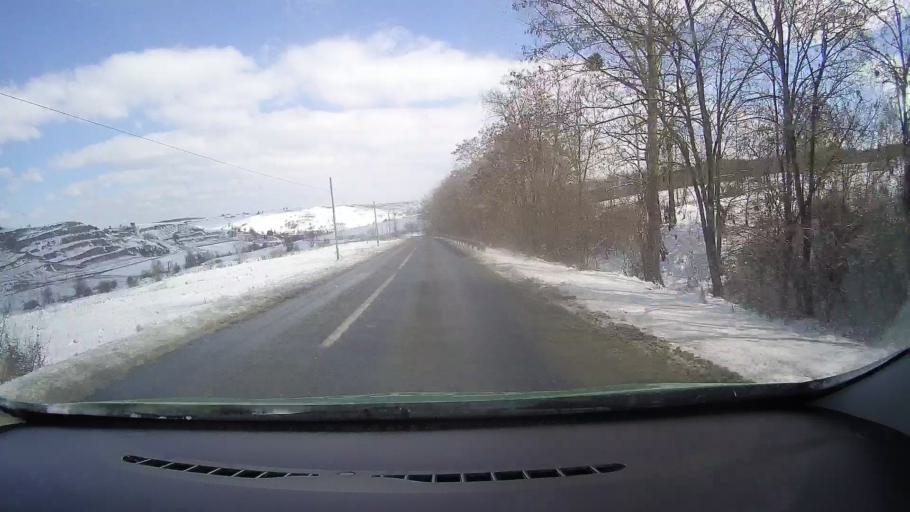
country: RO
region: Sibiu
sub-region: Comuna Barghis
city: Barghis
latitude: 45.9793
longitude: 24.5196
